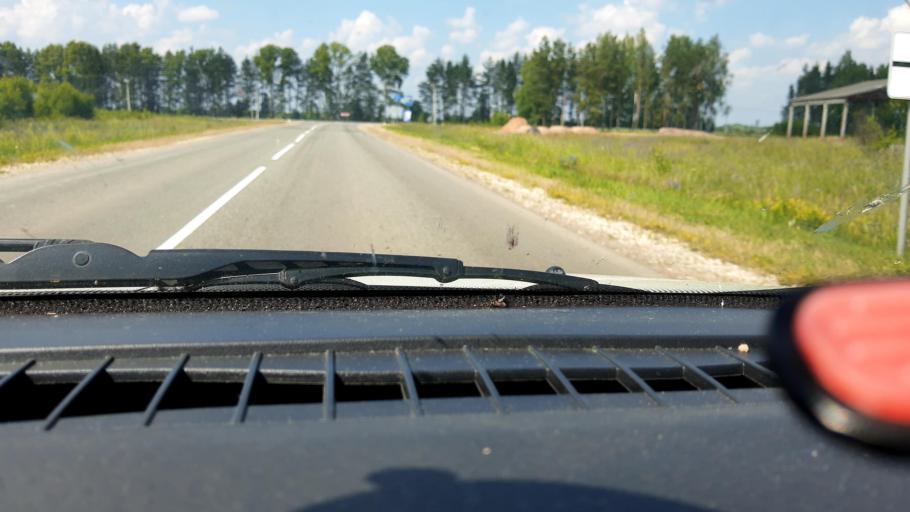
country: RU
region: Nizjnij Novgorod
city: Tonkino
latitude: 57.3708
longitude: 46.4208
